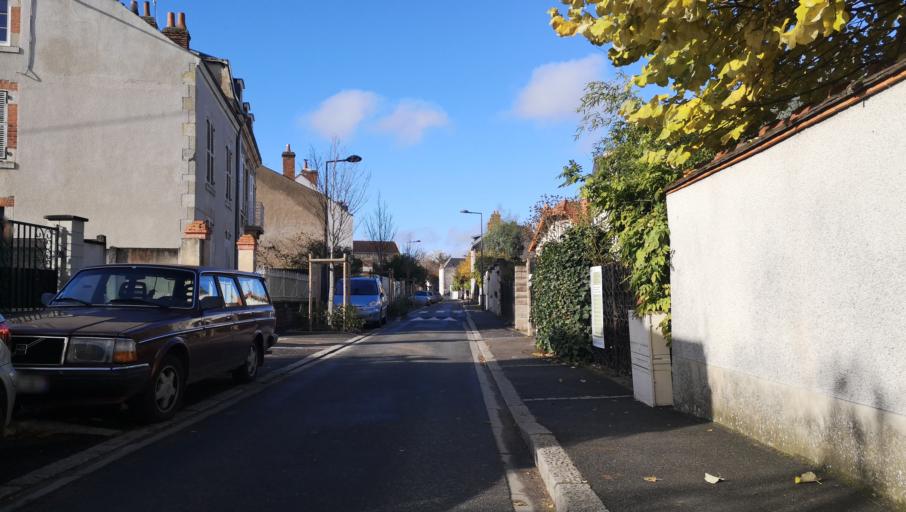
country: FR
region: Centre
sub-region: Departement du Loiret
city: Saint-Jean-le-Blanc
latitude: 47.9049
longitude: 1.9288
